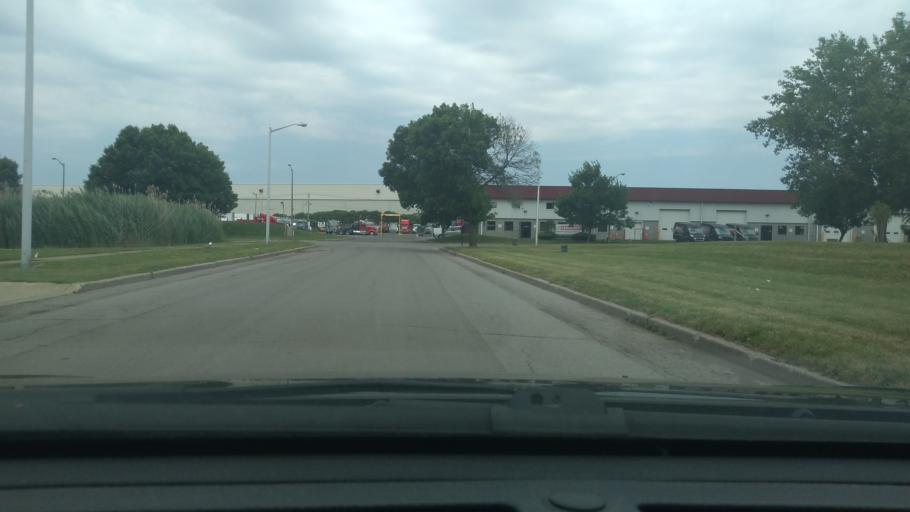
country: US
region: New York
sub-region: Erie County
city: Lackawanna
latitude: 42.8304
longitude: -78.8490
